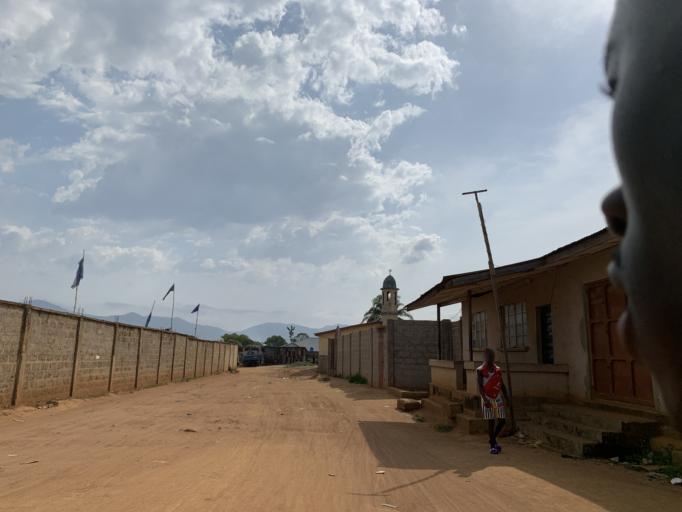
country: SL
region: Western Area
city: Waterloo
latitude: 8.3378
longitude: -13.0400
